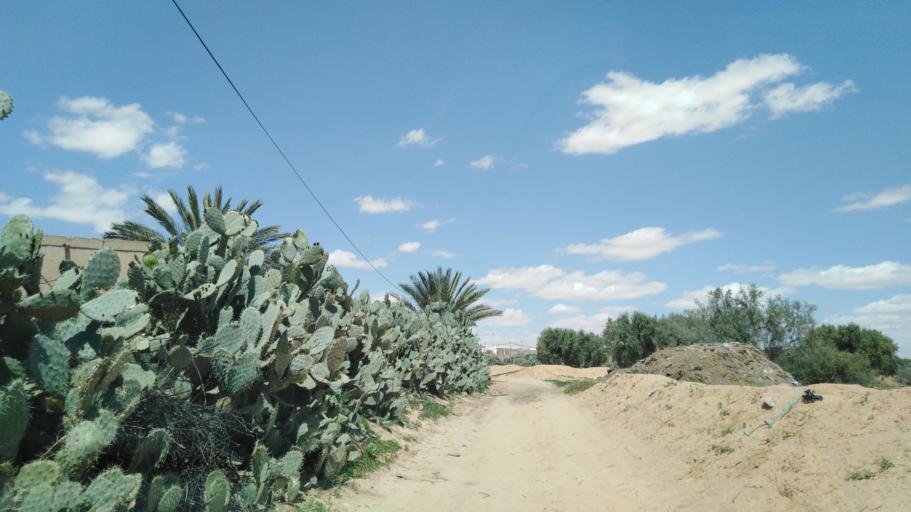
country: TN
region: Safaqis
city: Sfax
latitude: 34.7473
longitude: 10.5393
